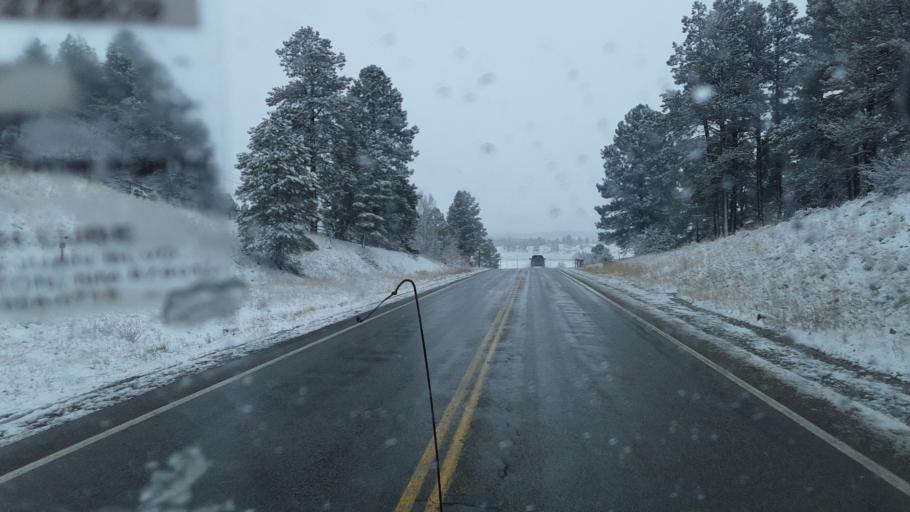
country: US
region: Colorado
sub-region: Archuleta County
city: Pagosa Springs
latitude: 37.2090
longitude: -106.9777
